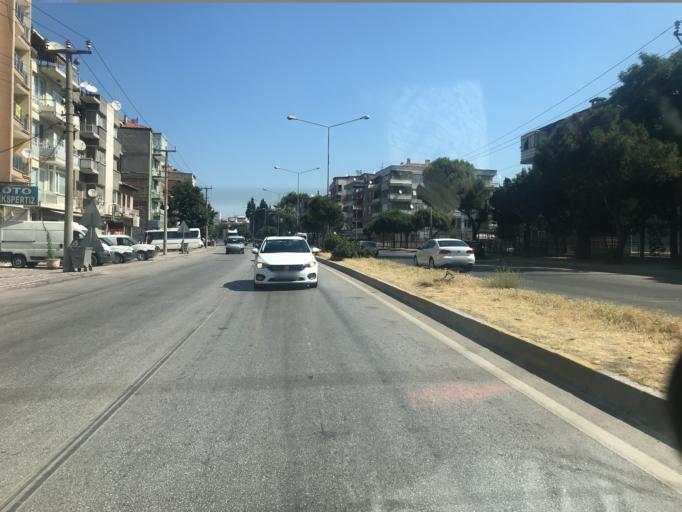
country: TR
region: Manisa
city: Akhisar
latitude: 38.9240
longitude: 27.8343
